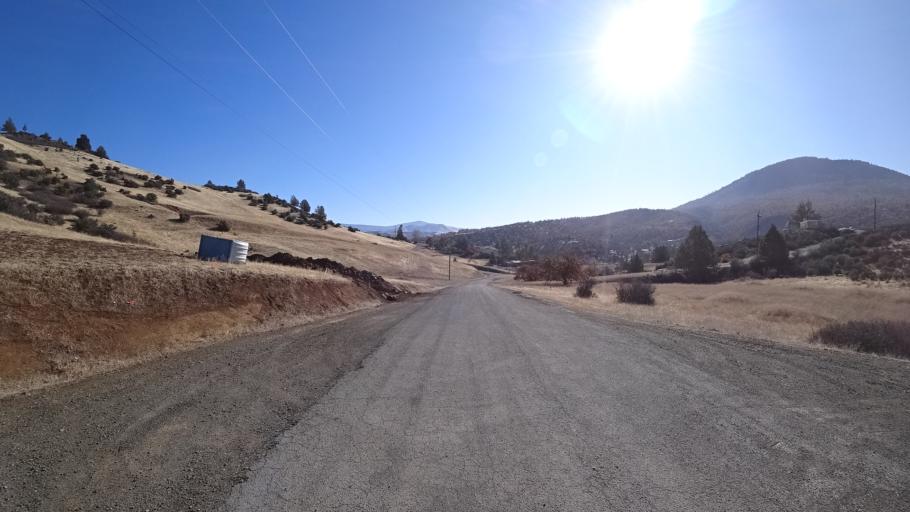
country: US
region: California
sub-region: Siskiyou County
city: Montague
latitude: 41.9004
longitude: -122.5245
